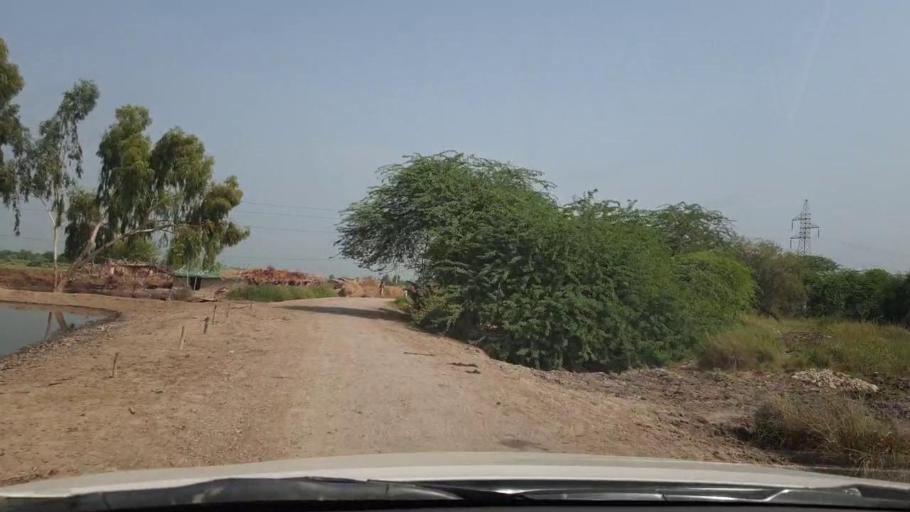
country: PK
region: Sindh
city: Shikarpur
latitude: 27.9724
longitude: 68.6706
